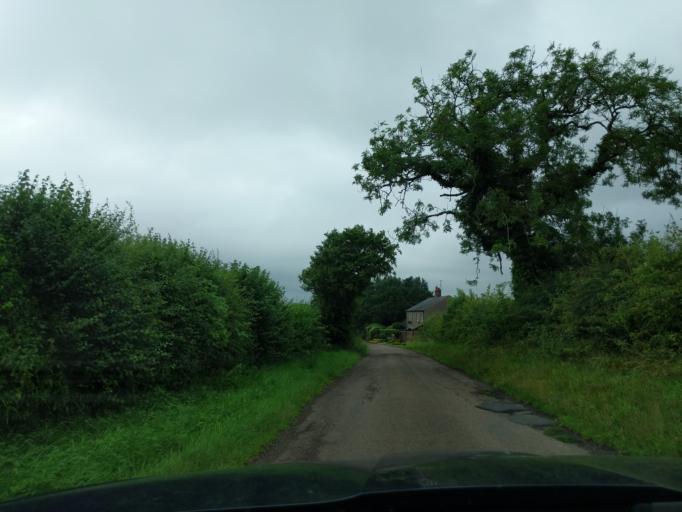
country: GB
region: England
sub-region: Northumberland
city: Ford
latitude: 55.6828
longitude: -2.1229
